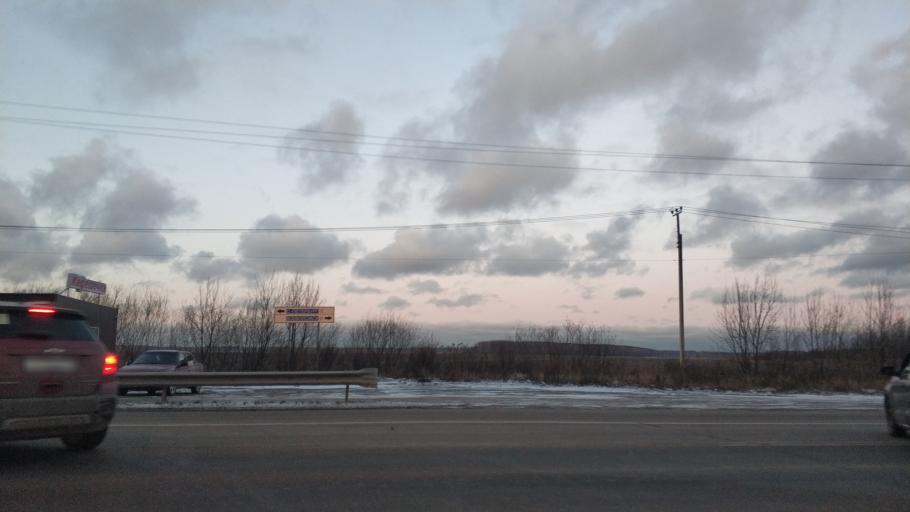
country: RU
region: St.-Petersburg
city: Pontonnyy
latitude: 59.8007
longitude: 30.6380
